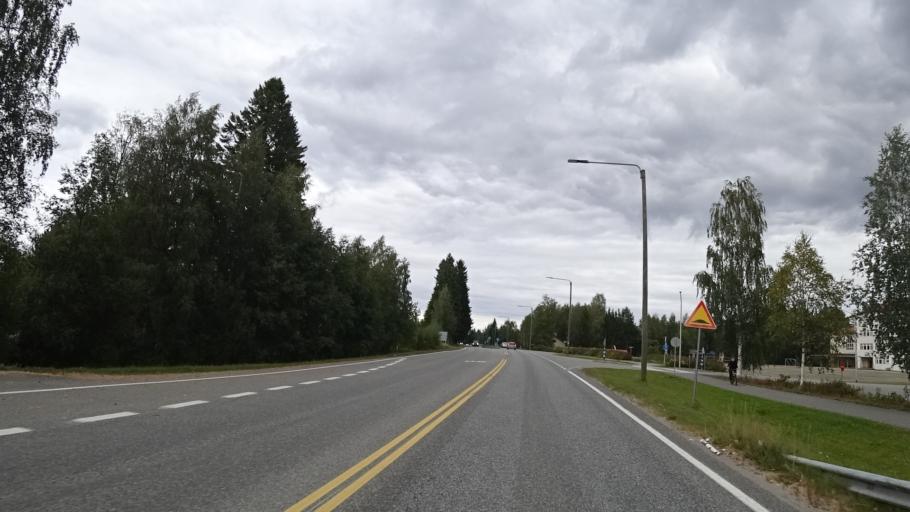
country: FI
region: North Karelia
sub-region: Joensuu
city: Ilomantsi
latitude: 62.6617
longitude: 30.9352
